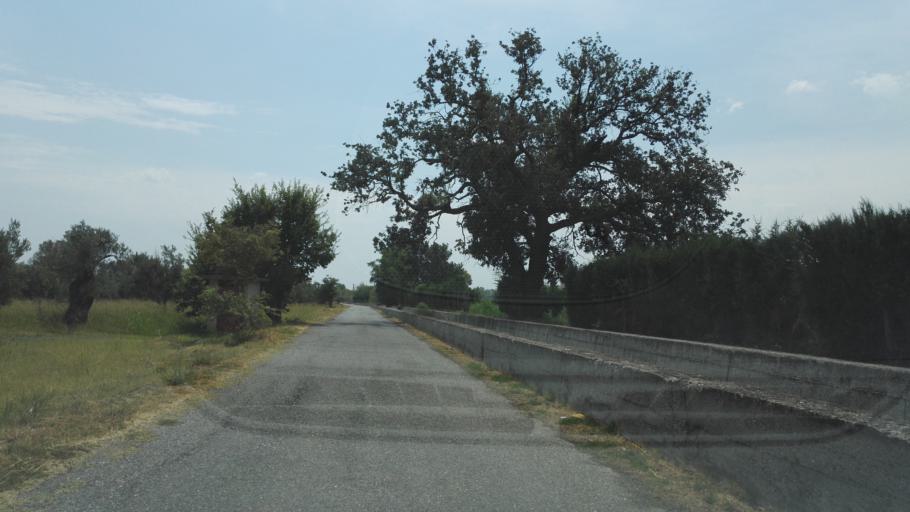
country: IT
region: Calabria
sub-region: Provincia di Reggio Calabria
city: Monasterace Marina
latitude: 38.4345
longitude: 16.5578
